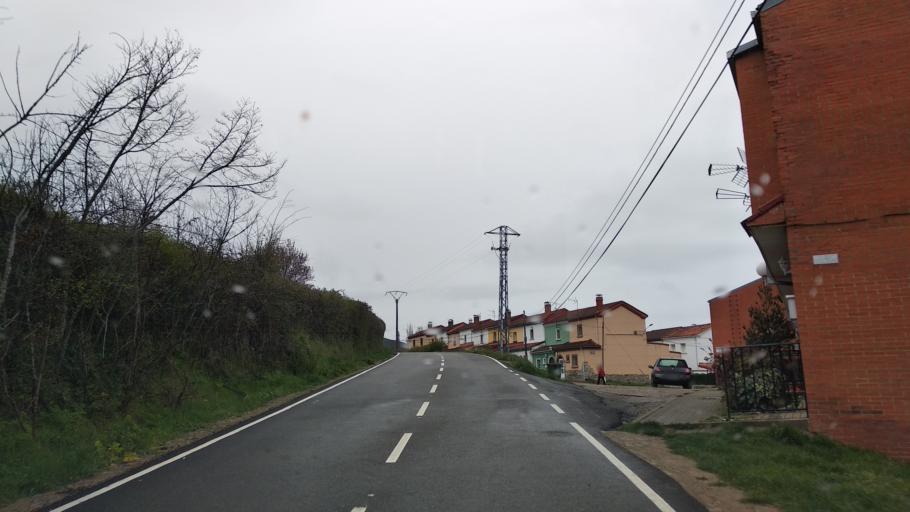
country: ES
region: Castille and Leon
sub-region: Provincia de Palencia
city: Barruelo de Santullan
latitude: 42.8995
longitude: -4.2863
